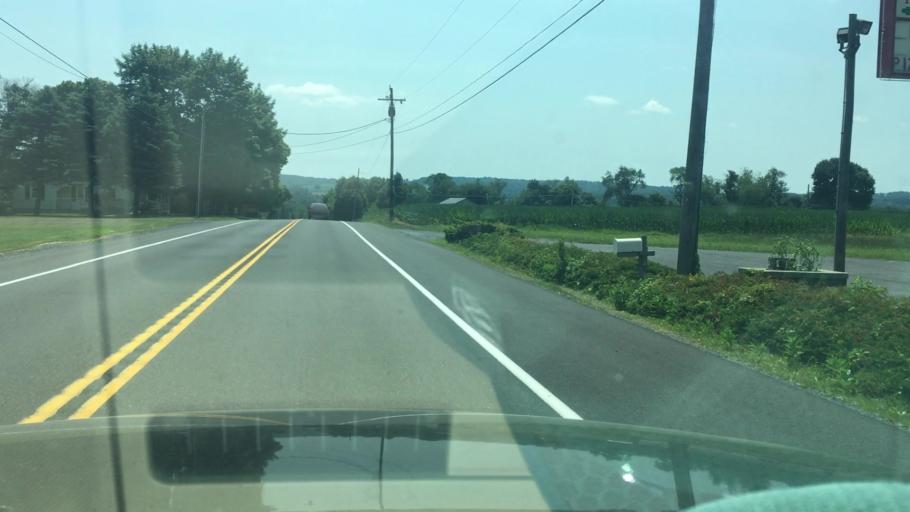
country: US
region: Pennsylvania
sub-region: Carbon County
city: Lehighton
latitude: 40.6941
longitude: -75.7509
